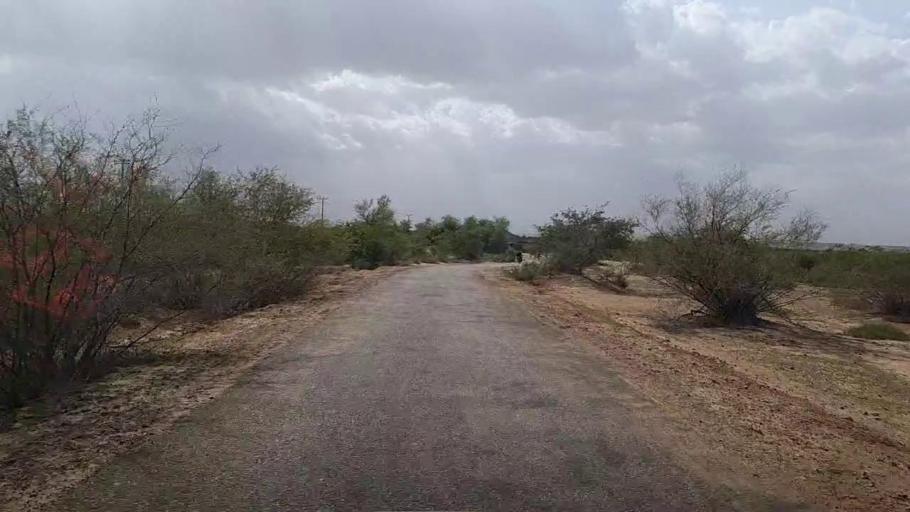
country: PK
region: Sindh
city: Jamshoro
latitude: 25.3980
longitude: 67.7175
